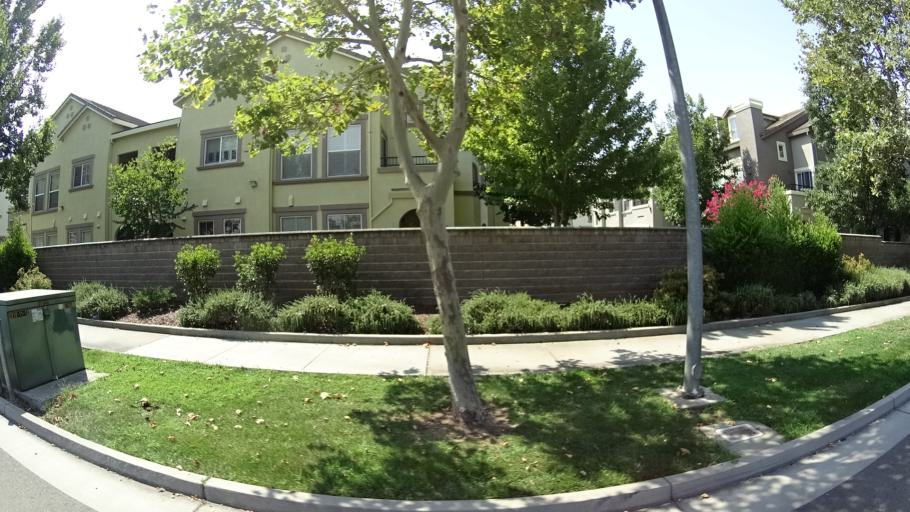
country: US
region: California
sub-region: Sacramento County
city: Laguna
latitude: 38.3938
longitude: -121.4389
